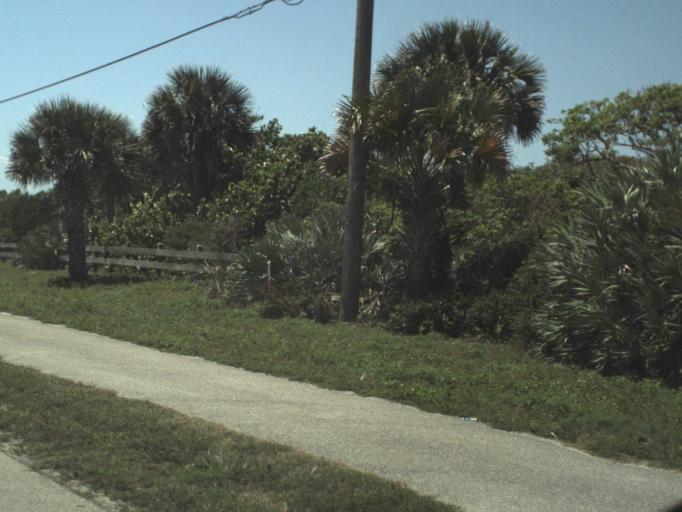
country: US
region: Florida
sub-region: Brevard County
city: Micco
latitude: 27.9033
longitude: -80.4724
